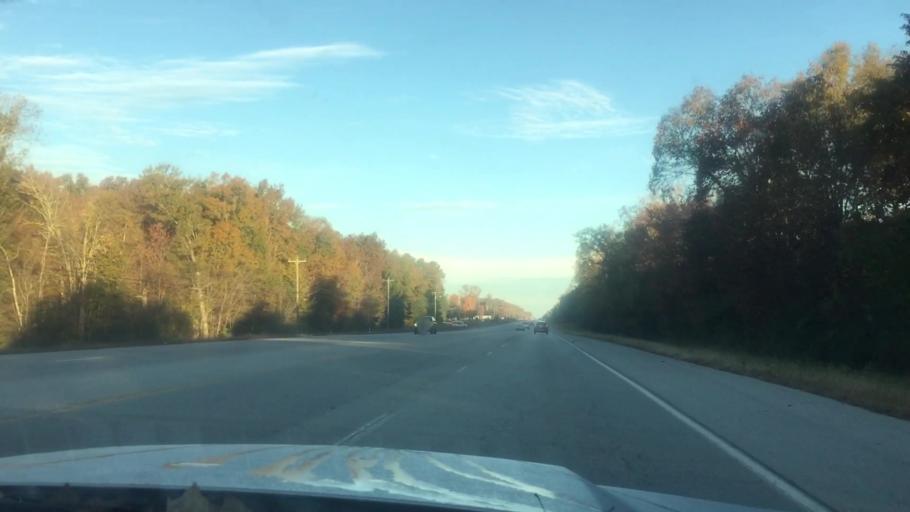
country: US
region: Tennessee
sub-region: Franklin County
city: Estill Springs
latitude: 35.2952
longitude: -86.1495
